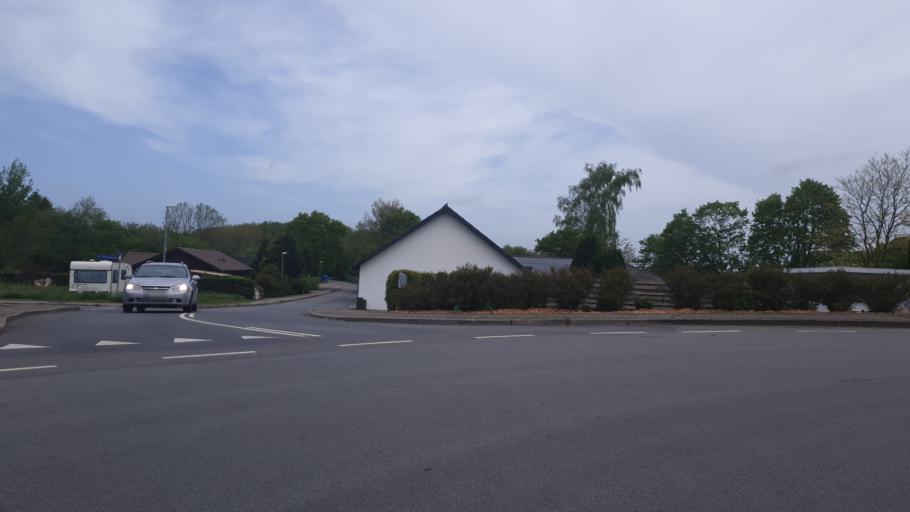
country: DK
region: Central Jutland
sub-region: Hedensted Kommune
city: Hedensted
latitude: 55.8045
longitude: 9.7019
